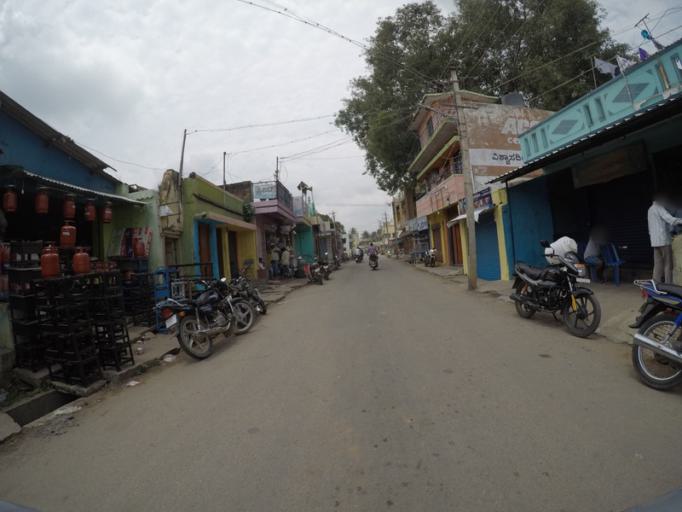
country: IN
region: Karnataka
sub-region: Ramanagara
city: Kanakapura
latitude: 12.5500
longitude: 77.4231
